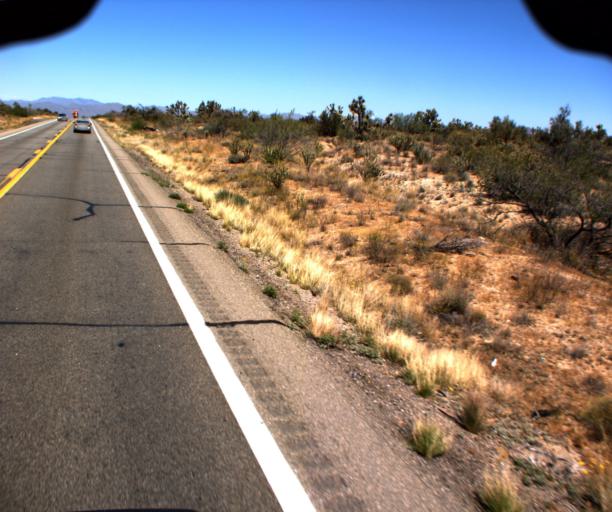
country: US
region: Arizona
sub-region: Yavapai County
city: Congress
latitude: 34.2623
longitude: -113.0891
